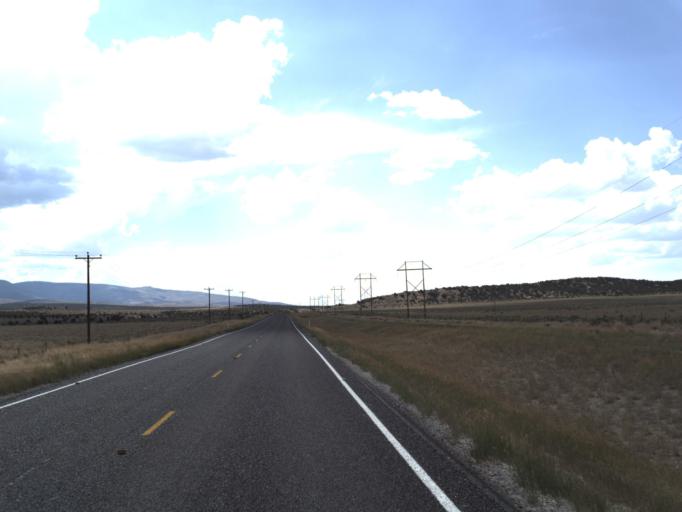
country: US
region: Idaho
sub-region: Minidoka County
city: Rupert
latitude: 41.9707
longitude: -113.1287
